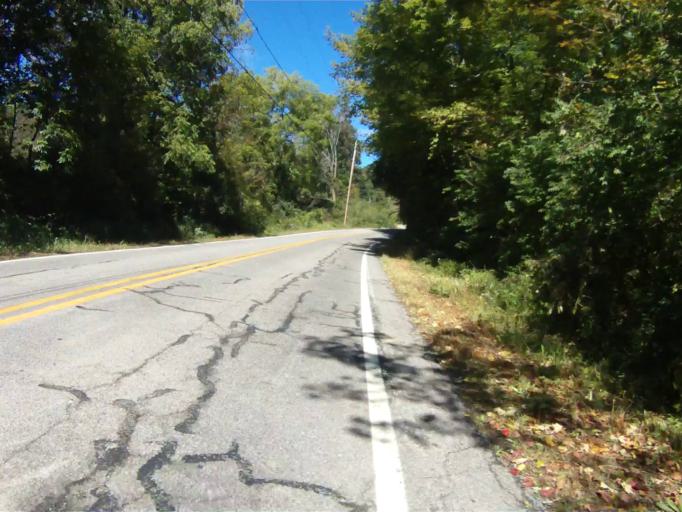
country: US
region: Pennsylvania
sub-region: Centre County
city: Park Forest Village
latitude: 40.8671
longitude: -77.8887
